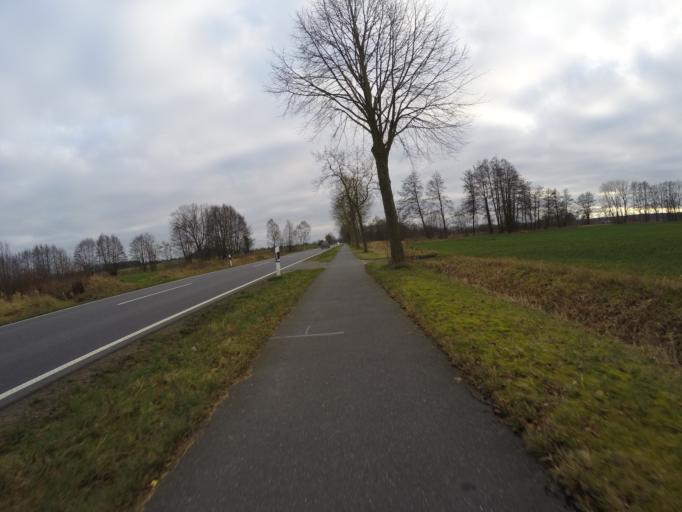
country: DE
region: Schleswig-Holstein
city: Alveslohe
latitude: 53.7668
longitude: 9.9073
